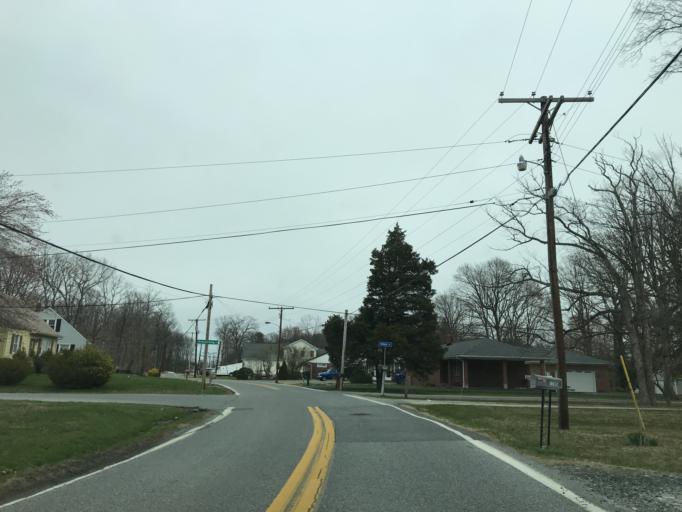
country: US
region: Maryland
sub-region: Baltimore County
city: Middle River
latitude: 39.2986
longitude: -76.4250
